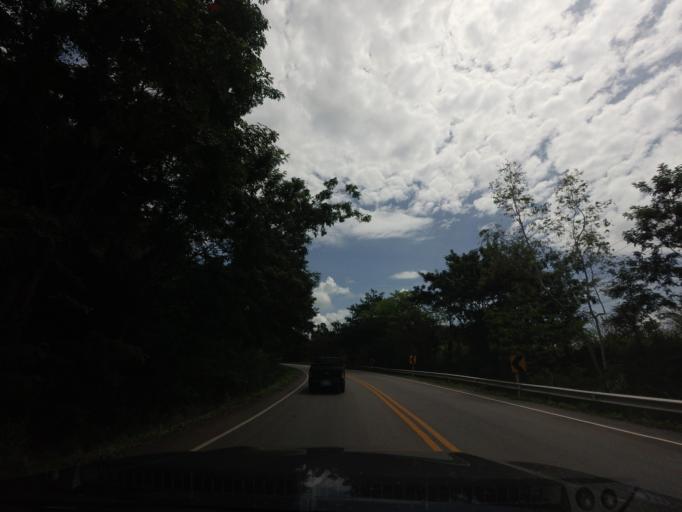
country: TH
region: Nong Khai
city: Pho Tak
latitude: 17.8031
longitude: 102.3205
